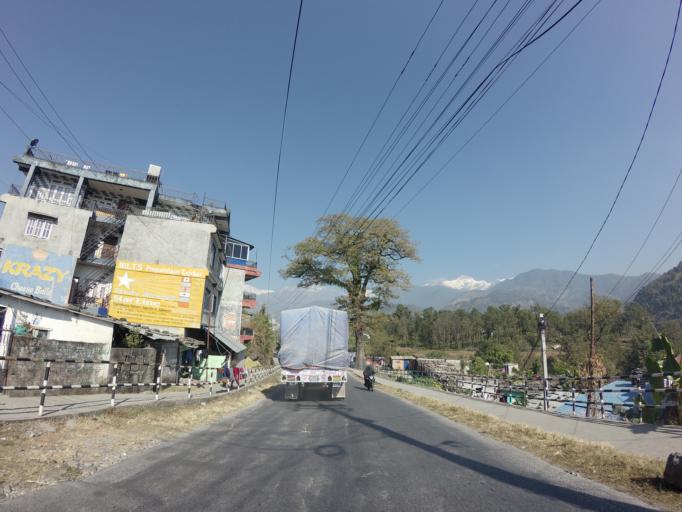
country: NP
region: Western Region
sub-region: Gandaki Zone
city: Pokhara
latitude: 28.2360
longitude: 83.9899
